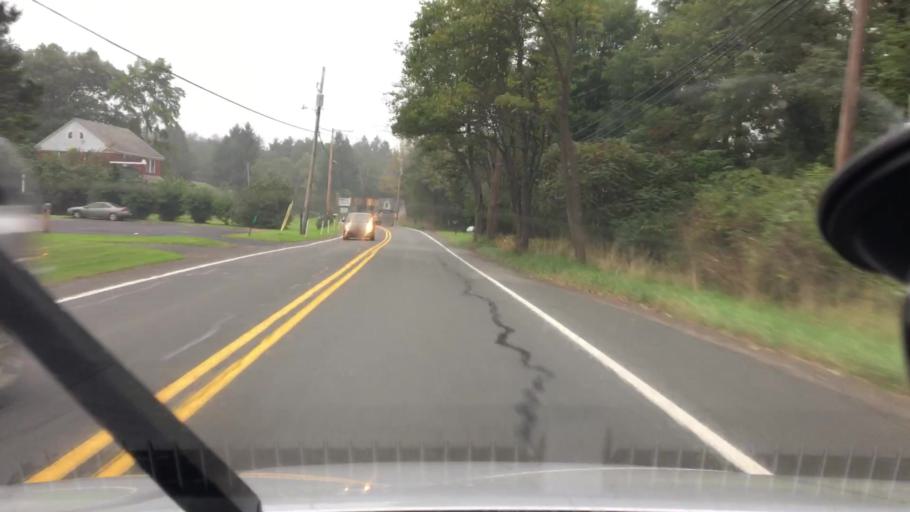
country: US
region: Pennsylvania
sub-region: Monroe County
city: Mountainhome
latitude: 41.1597
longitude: -75.2791
